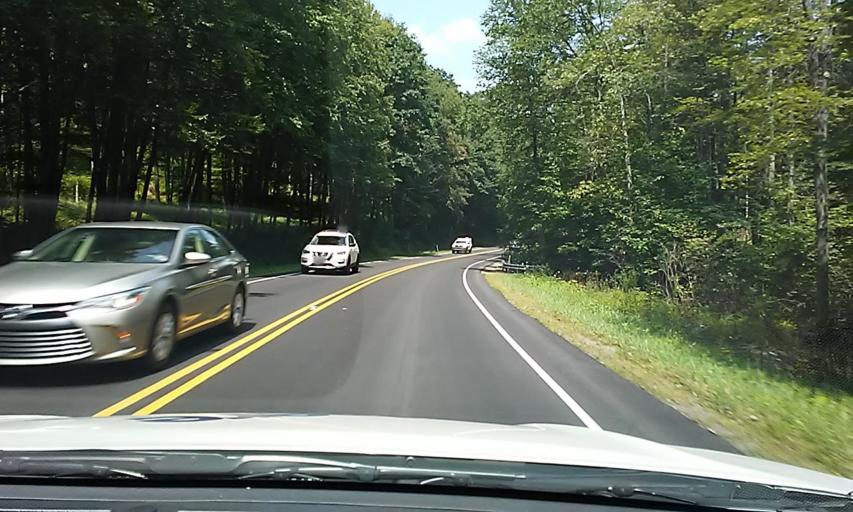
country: US
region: Pennsylvania
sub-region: Elk County
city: Saint Marys
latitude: 41.4628
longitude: -78.4274
